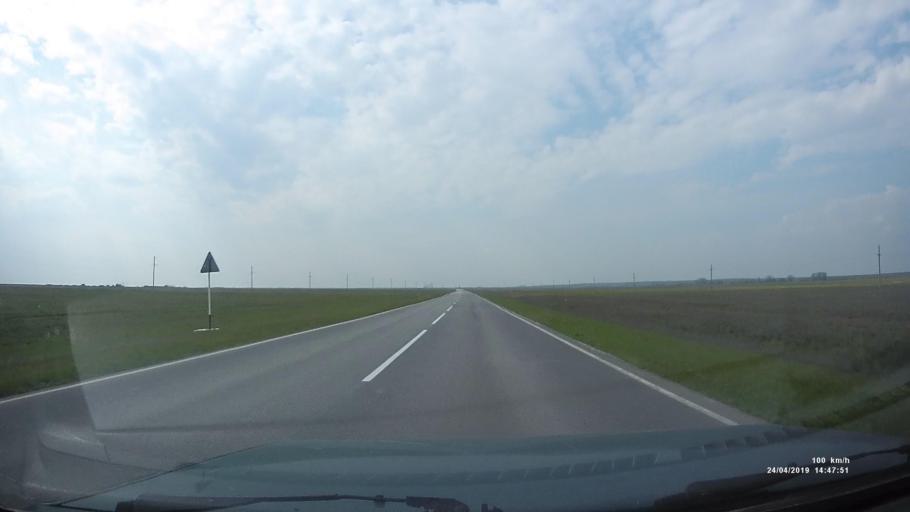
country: RU
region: Rostov
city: Remontnoye
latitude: 46.4953
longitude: 43.7661
